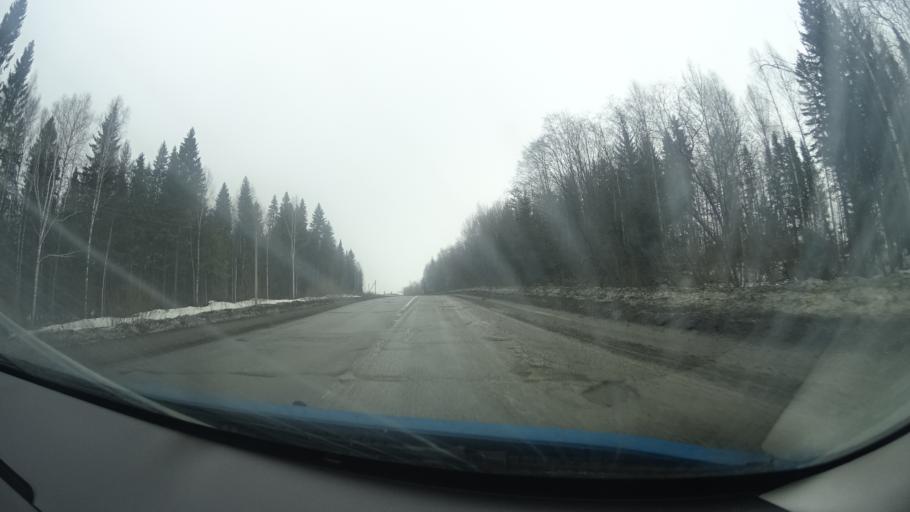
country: RU
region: Bashkortostan
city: Verkhniye Tatyshly
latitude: 56.4825
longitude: 55.7908
